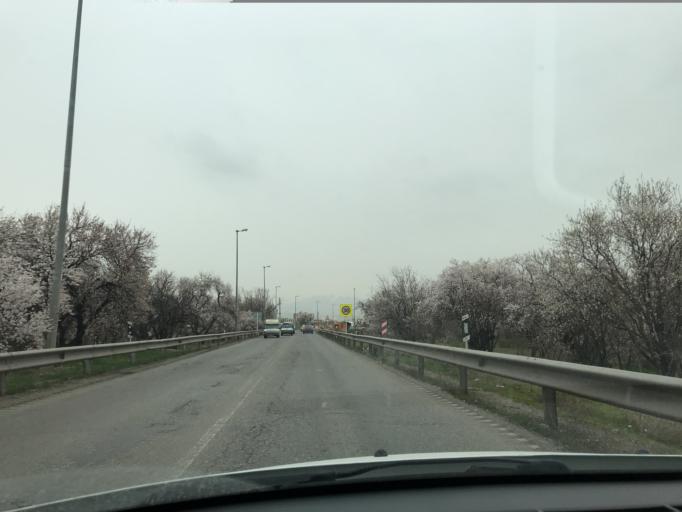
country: IR
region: Qazvin
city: Qazvin
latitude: 36.2803
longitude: 49.9849
